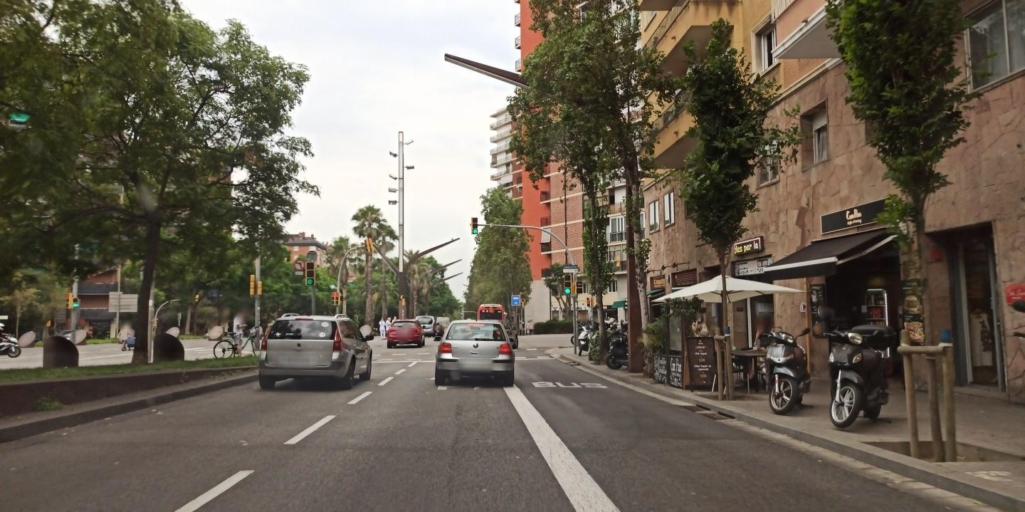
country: ES
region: Catalonia
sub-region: Provincia de Barcelona
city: les Corts
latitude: 41.3828
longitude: 2.1278
